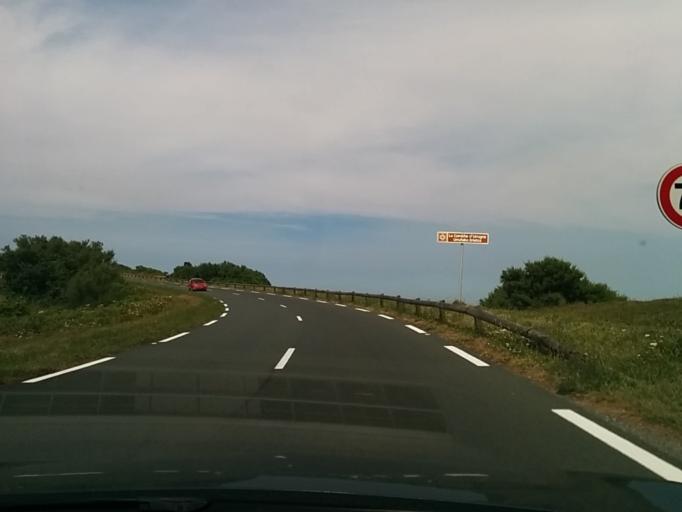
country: FR
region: Aquitaine
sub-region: Departement des Pyrenees-Atlantiques
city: Ciboure
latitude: 43.3942
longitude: -1.6889
